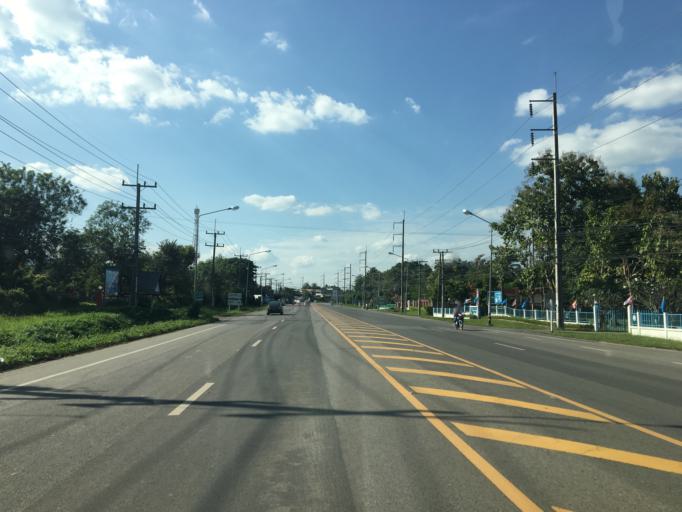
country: TH
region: Phayao
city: Chun
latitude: 19.3369
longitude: 100.1327
